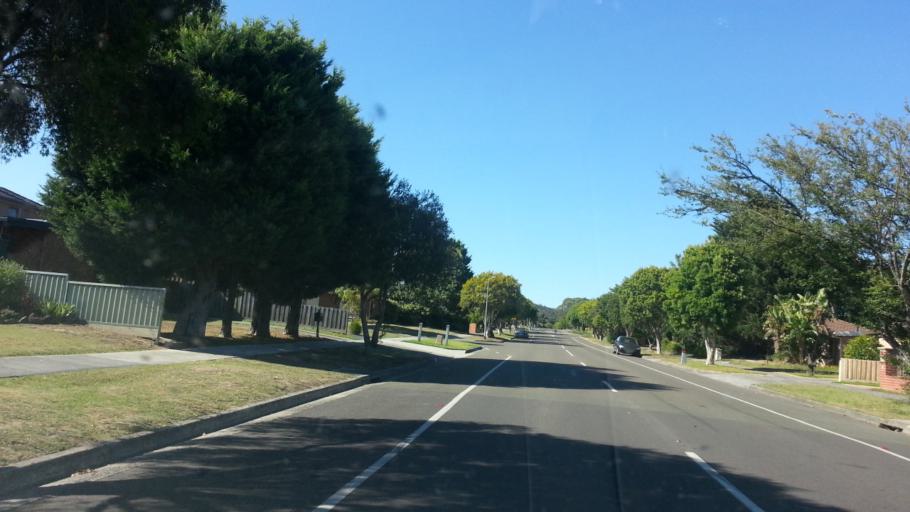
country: AU
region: Victoria
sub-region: Knox
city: Knoxfield
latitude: -37.9175
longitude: 145.2695
